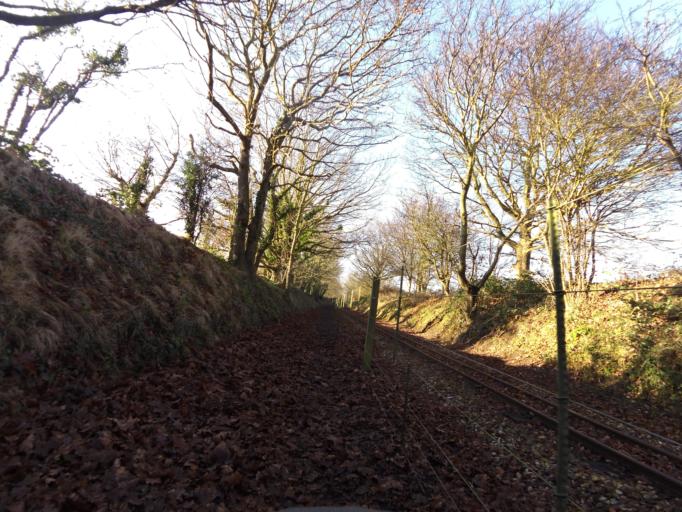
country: GB
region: England
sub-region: Norfolk
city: Coltishall
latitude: 52.7340
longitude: 1.3692
